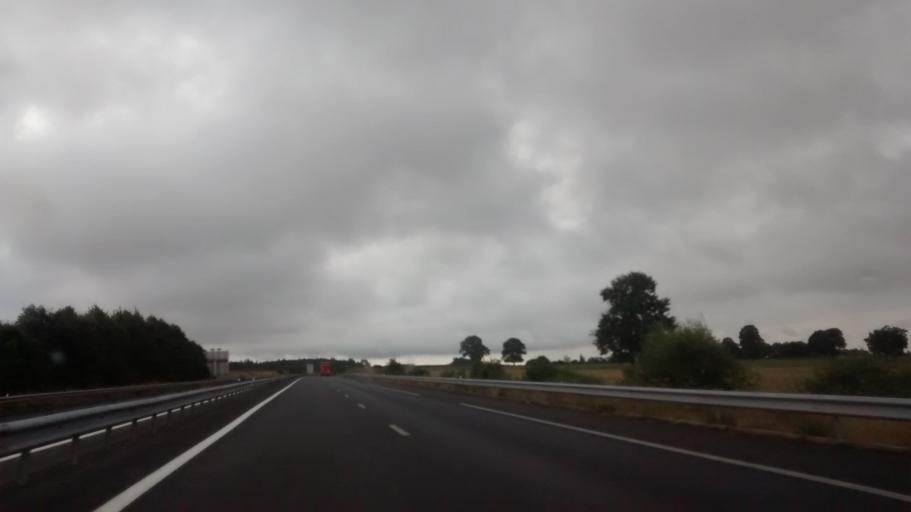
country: FR
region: Brittany
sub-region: Departement d'Ille-et-Vilaine
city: Saint-Sauveur-des-Landes
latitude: 48.3544
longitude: -1.3013
